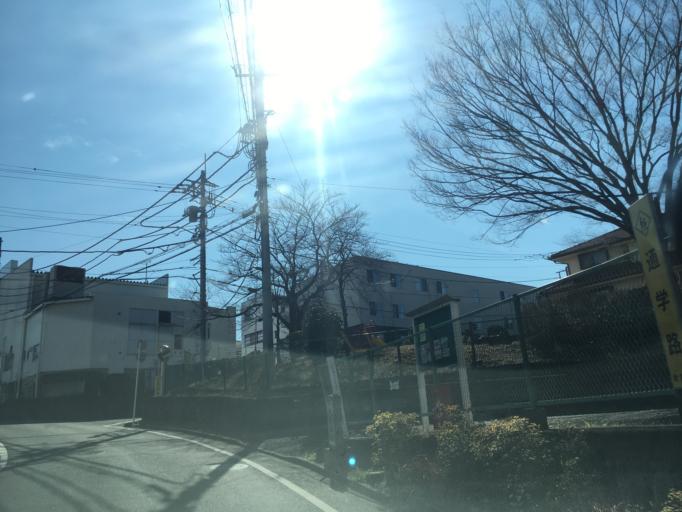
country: JP
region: Tokyo
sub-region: Machida-shi
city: Machida
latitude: 35.5813
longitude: 139.4168
